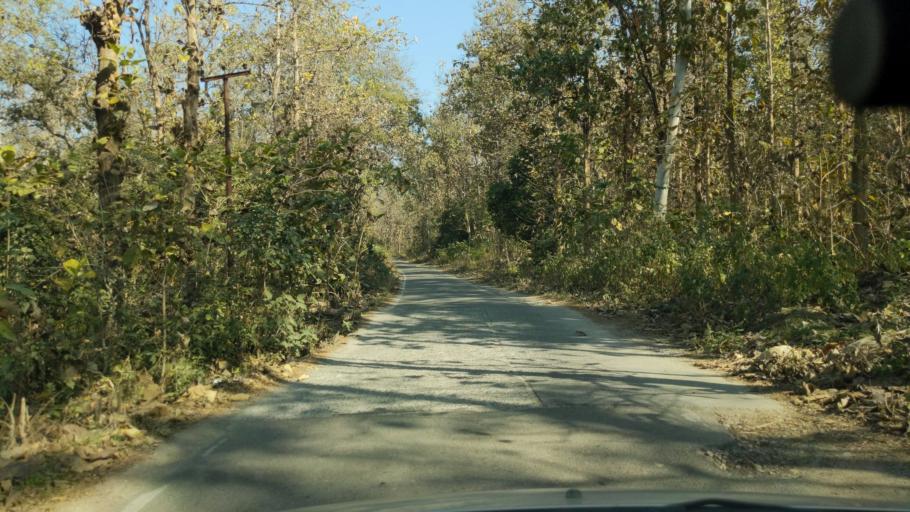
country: IN
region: Uttarakhand
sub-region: Naini Tal
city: Ramnagar
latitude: 29.4036
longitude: 79.1370
